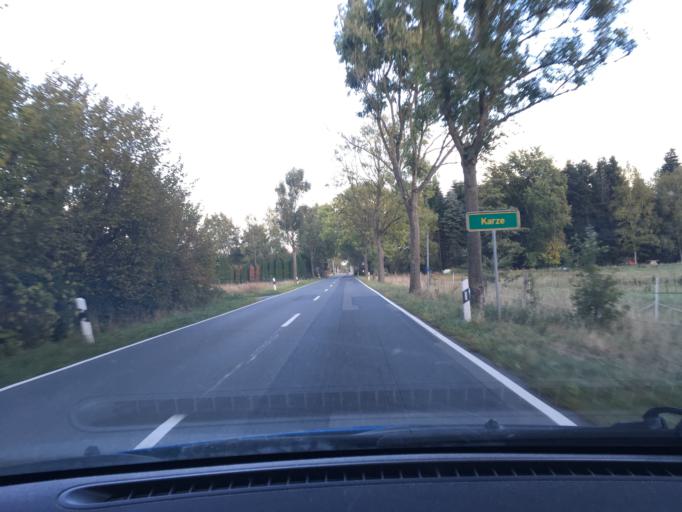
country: DE
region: Lower Saxony
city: Neetze
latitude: 53.3160
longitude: 10.6600
